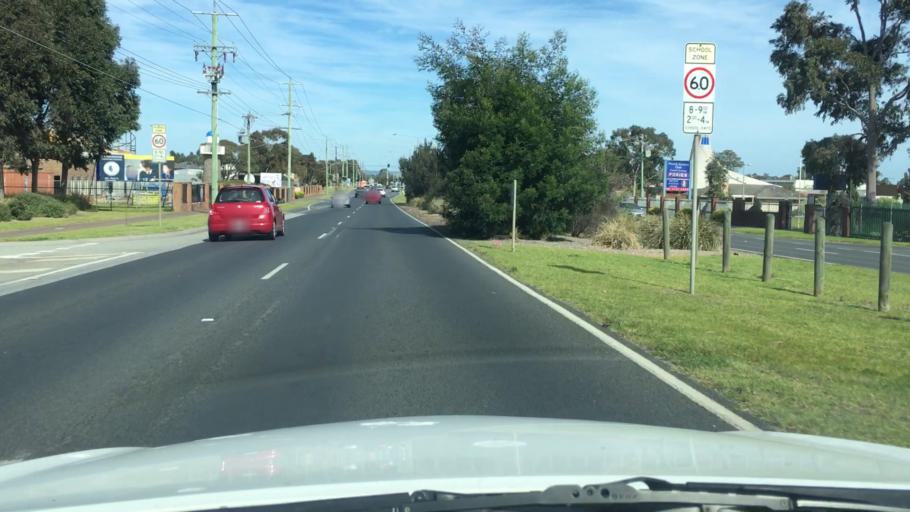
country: AU
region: Victoria
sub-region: Kingston
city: Dingley Village
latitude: -37.9999
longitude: 145.1430
